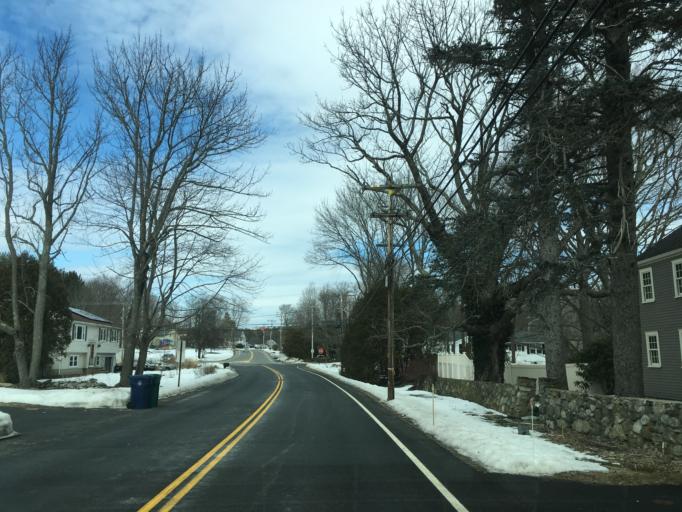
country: US
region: New Hampshire
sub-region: Rockingham County
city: Hampton
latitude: 42.9374
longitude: -70.8187
